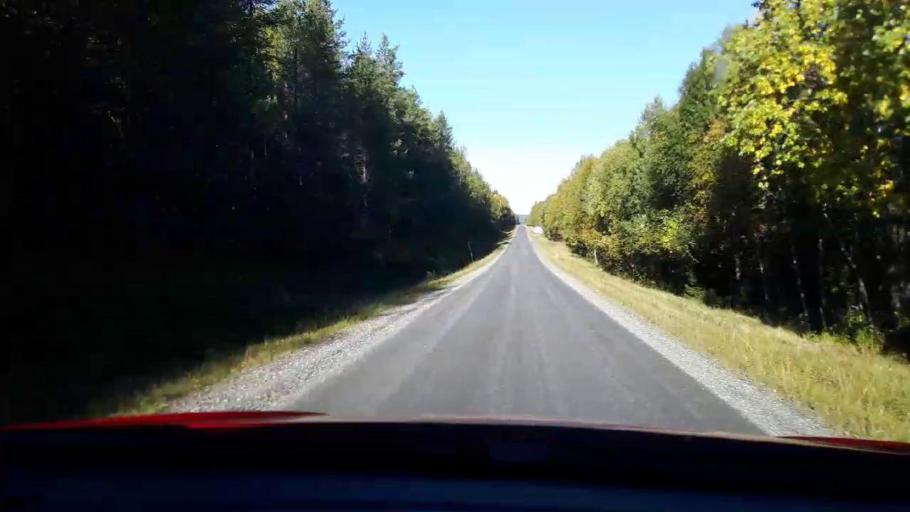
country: NO
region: Nord-Trondelag
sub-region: Lierne
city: Sandvika
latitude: 64.5398
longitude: 14.0038
